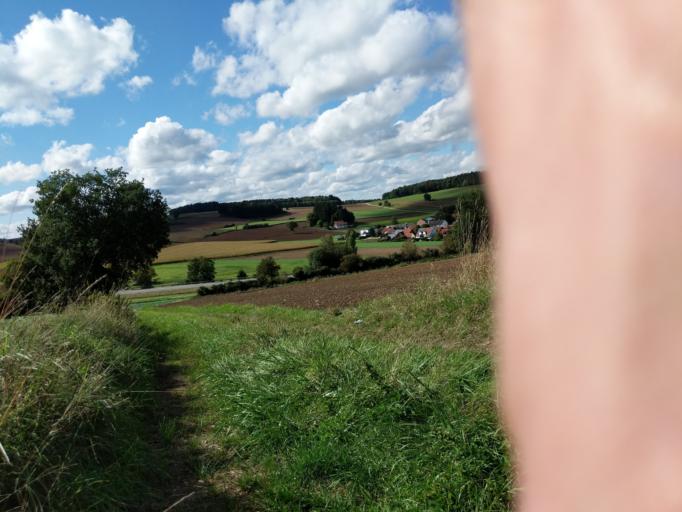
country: DE
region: Bavaria
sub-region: Lower Bavaria
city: Bad Abbach
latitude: 48.9526
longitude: 12.0465
